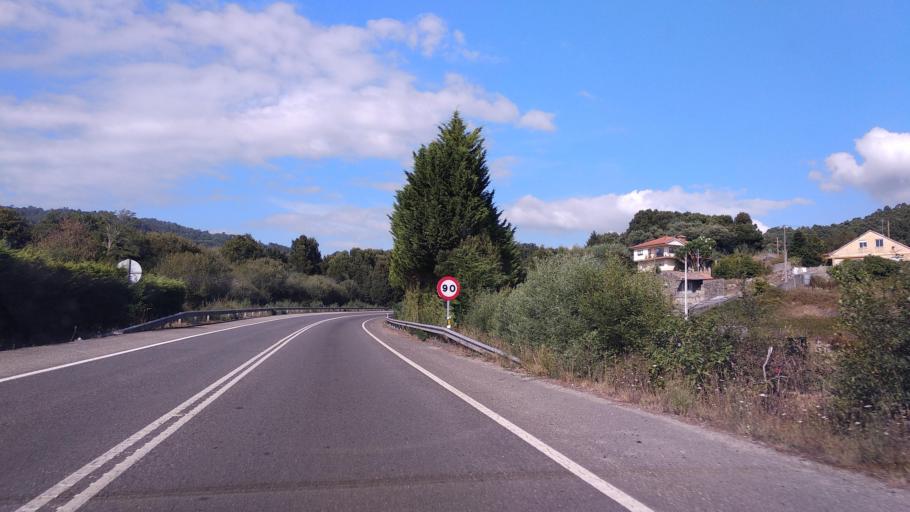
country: ES
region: Galicia
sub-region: Provincia de Pontevedra
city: Cangas
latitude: 42.2693
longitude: -8.7650
